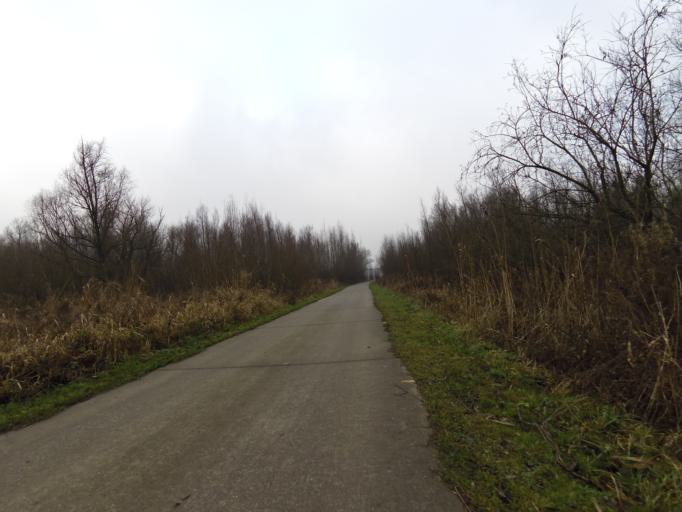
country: NL
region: South Holland
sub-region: Gemeente Oud-Beijerland
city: Oud-Beijerland
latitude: 51.8386
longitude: 4.3932
